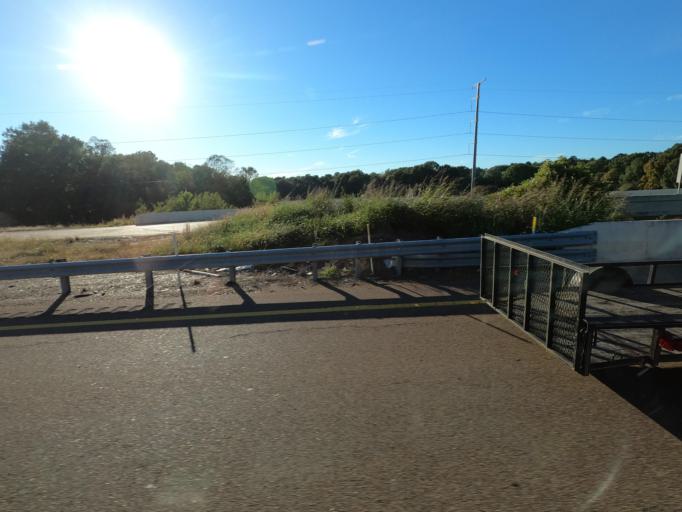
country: US
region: Tennessee
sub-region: Fayette County
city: Piperton
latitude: 35.0559
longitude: -89.6372
